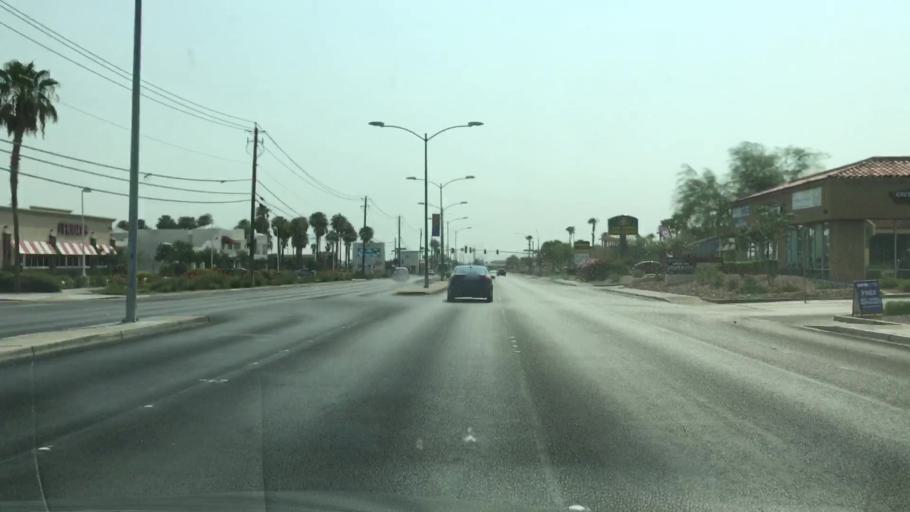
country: US
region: Nevada
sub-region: Clark County
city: Whitney
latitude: 36.0708
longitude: -115.0805
